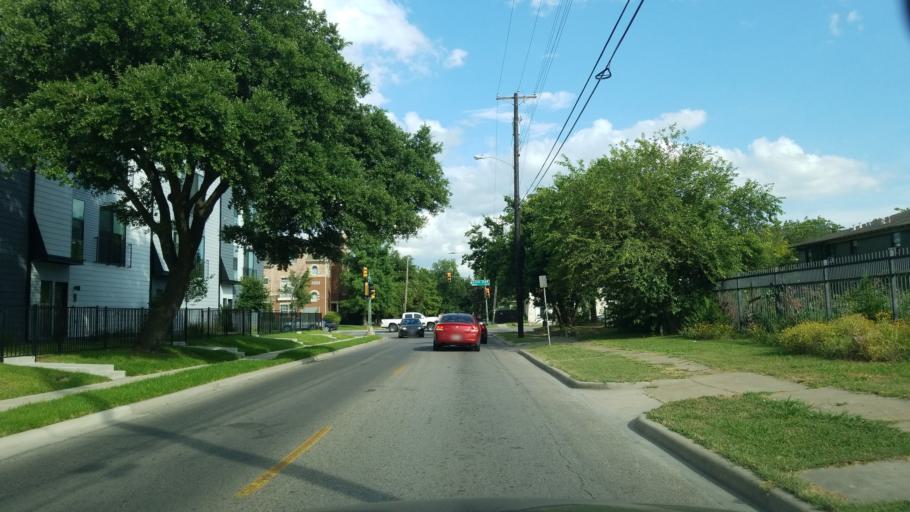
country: US
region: Texas
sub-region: Dallas County
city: Highland Park
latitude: 32.8032
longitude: -96.7729
